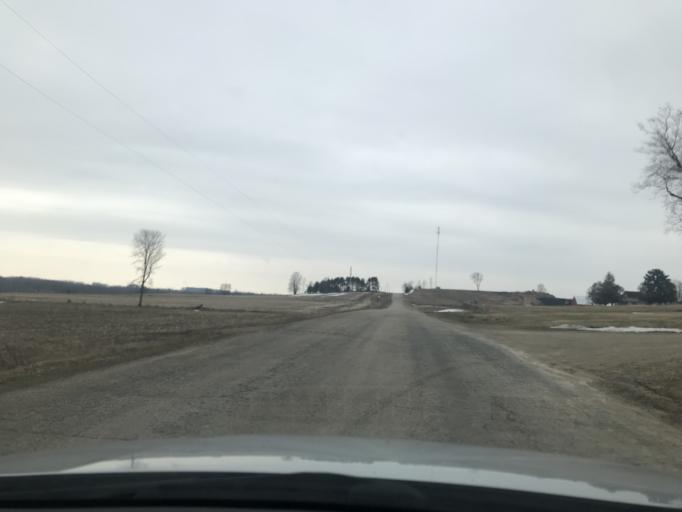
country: US
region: Wisconsin
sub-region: Marinette County
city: Peshtigo
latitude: 45.1015
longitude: -87.9323
